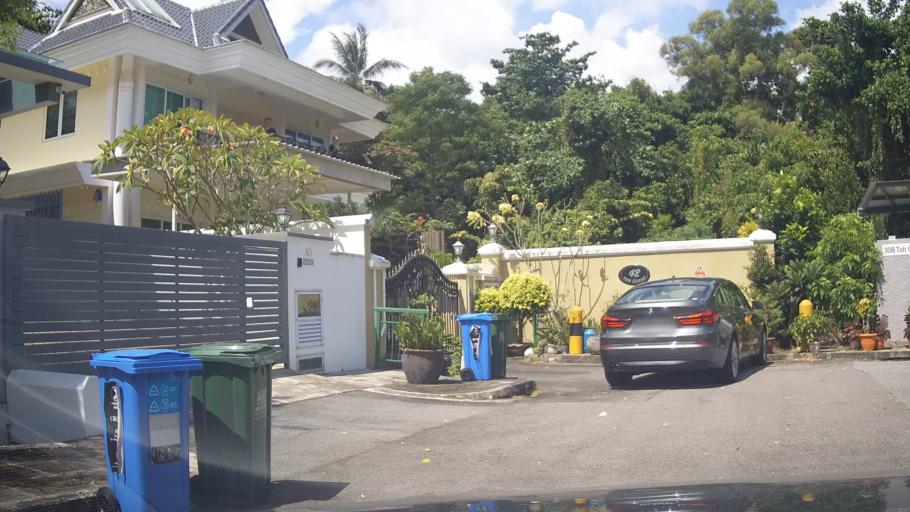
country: SG
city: Singapore
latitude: 1.3639
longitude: 103.9703
